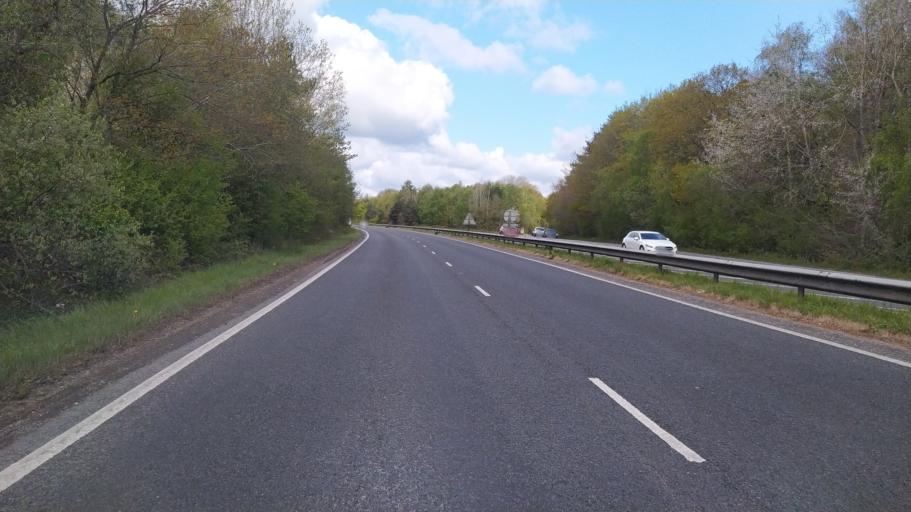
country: GB
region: England
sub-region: Hampshire
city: Totton
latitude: 50.8986
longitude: -1.4810
